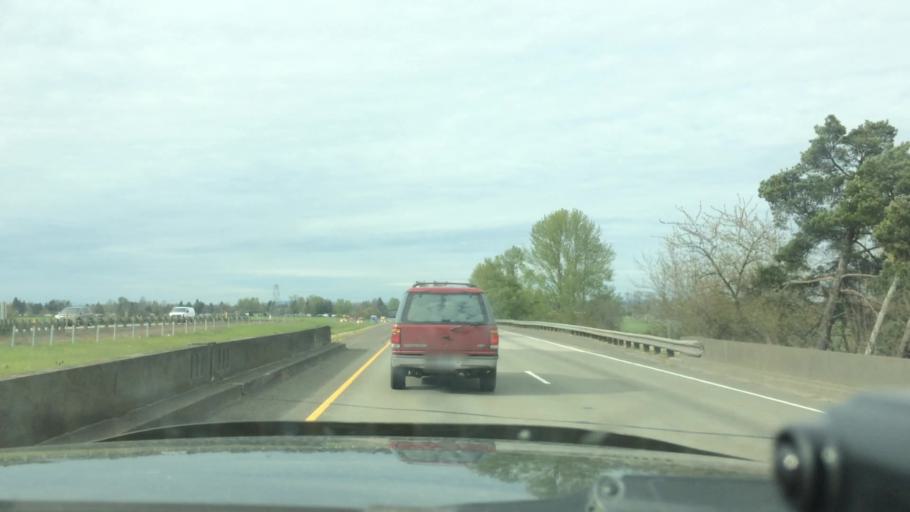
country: US
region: Oregon
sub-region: Linn County
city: Albany
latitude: 44.5959
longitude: -123.0619
